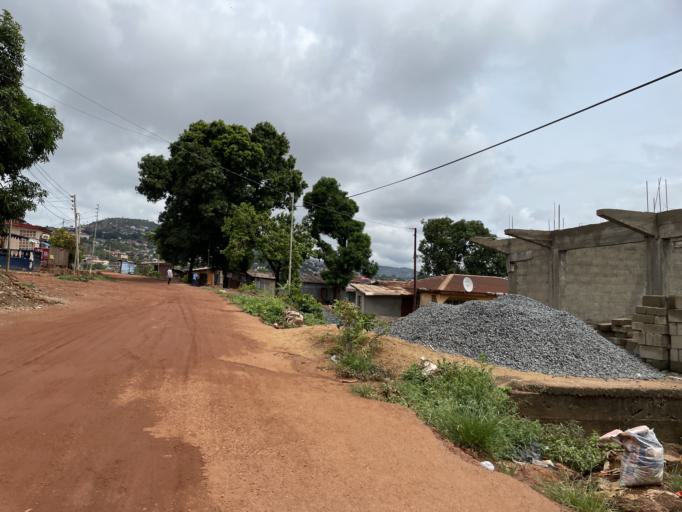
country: SL
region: Western Area
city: Hastings
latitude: 8.4127
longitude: -13.1470
